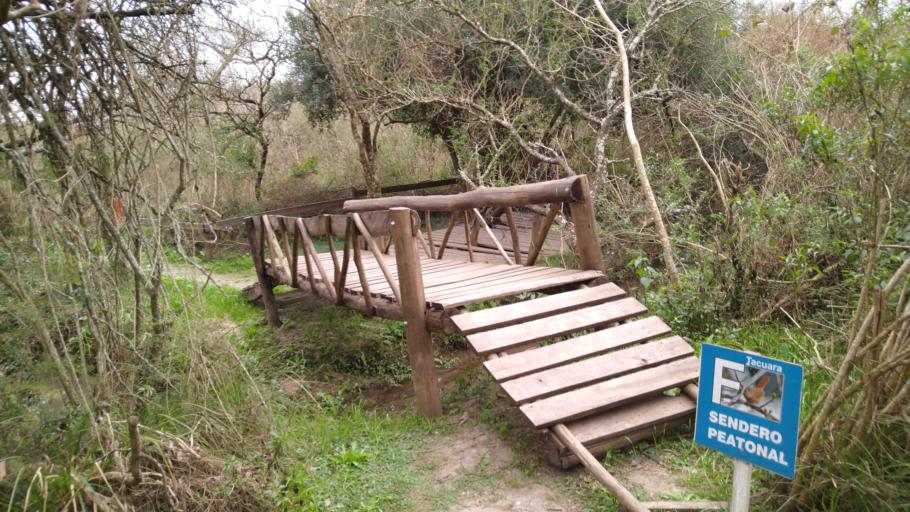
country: AR
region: Entre Rios
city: Chajari
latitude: -30.7403
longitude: -58.0134
